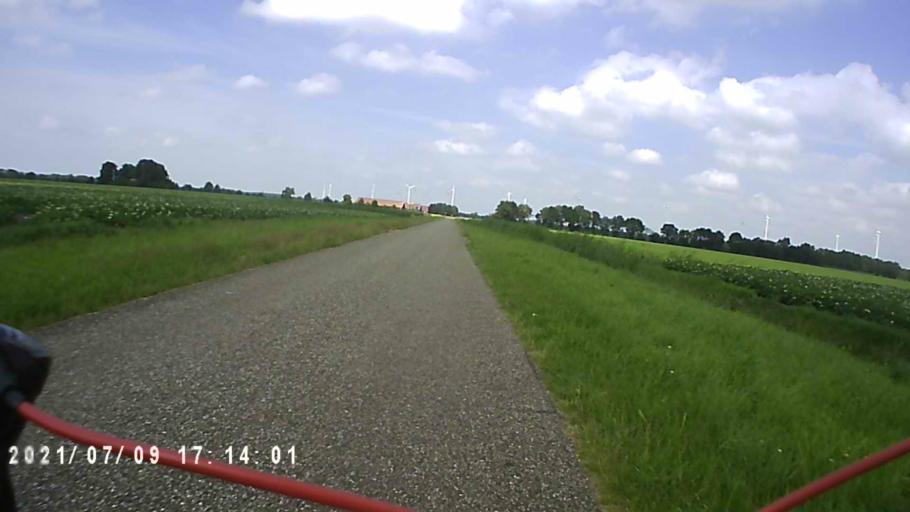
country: DE
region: Lower Saxony
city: Rhede
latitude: 53.0844
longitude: 7.1840
